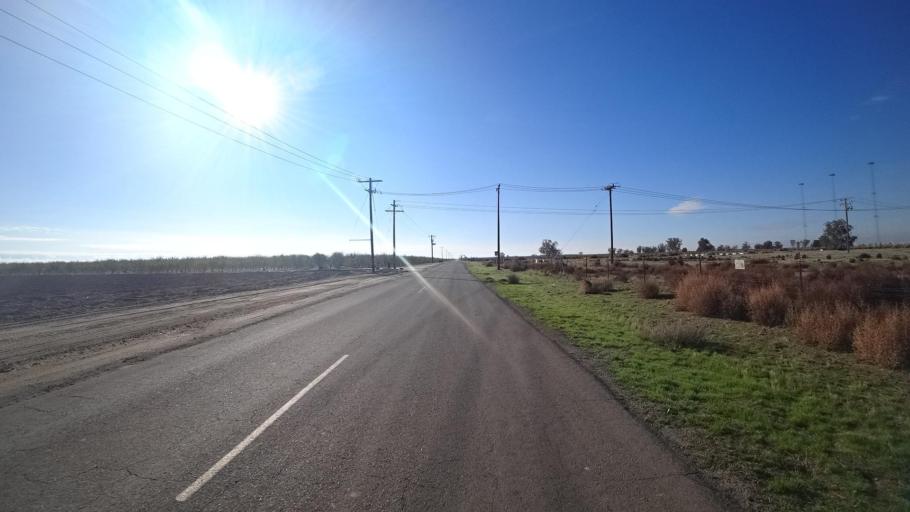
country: US
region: California
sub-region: Kern County
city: Delano
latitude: 35.7549
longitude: -119.2765
